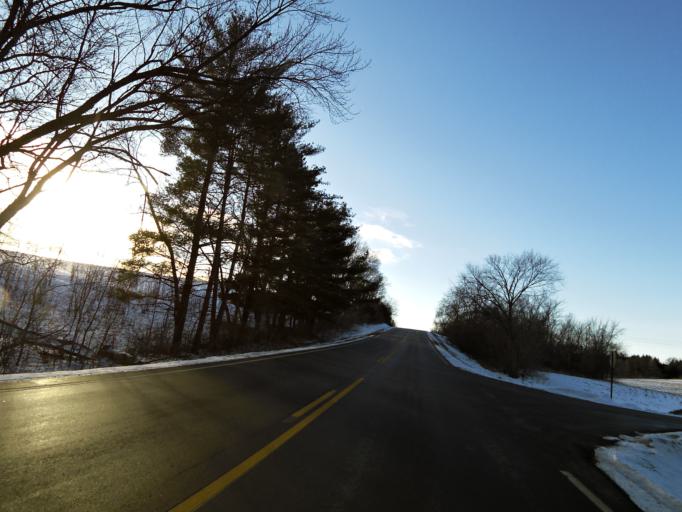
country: US
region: Wisconsin
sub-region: Pierce County
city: Prescott
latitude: 44.7902
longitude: -92.8270
